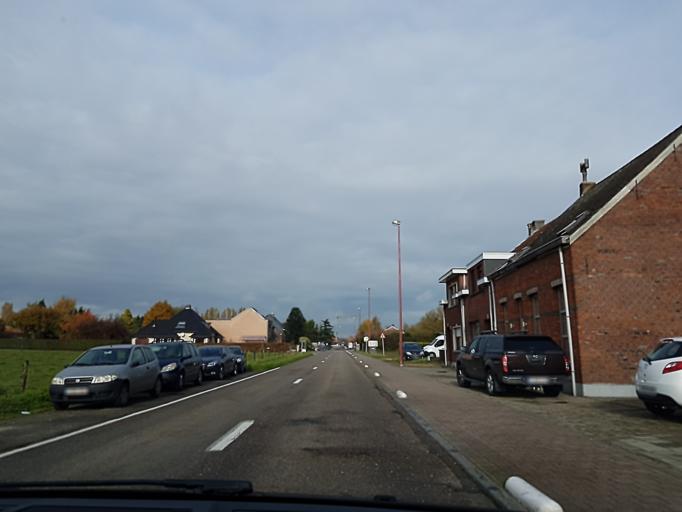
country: BE
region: Flanders
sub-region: Provincie Antwerpen
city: Lint
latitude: 51.1177
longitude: 4.4947
